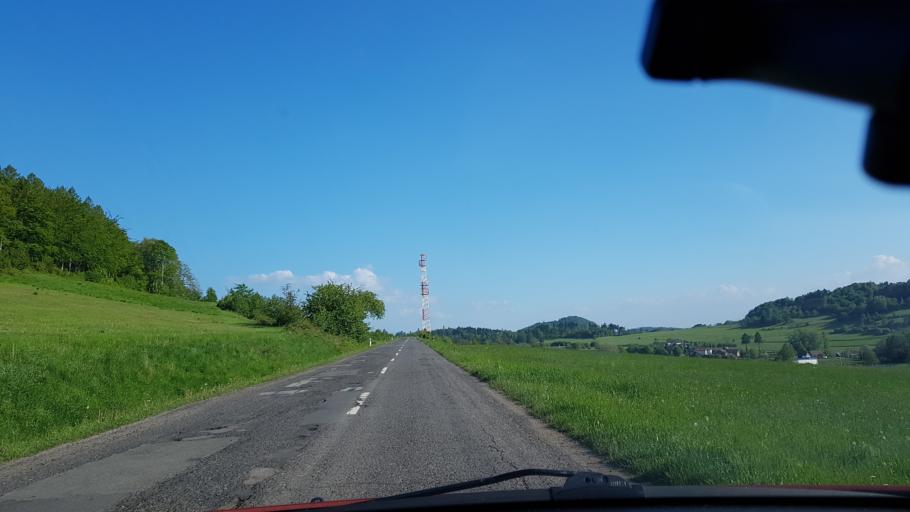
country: PL
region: Lower Silesian Voivodeship
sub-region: Powiat klodzki
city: Bozkow
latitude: 50.5835
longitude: 16.5845
